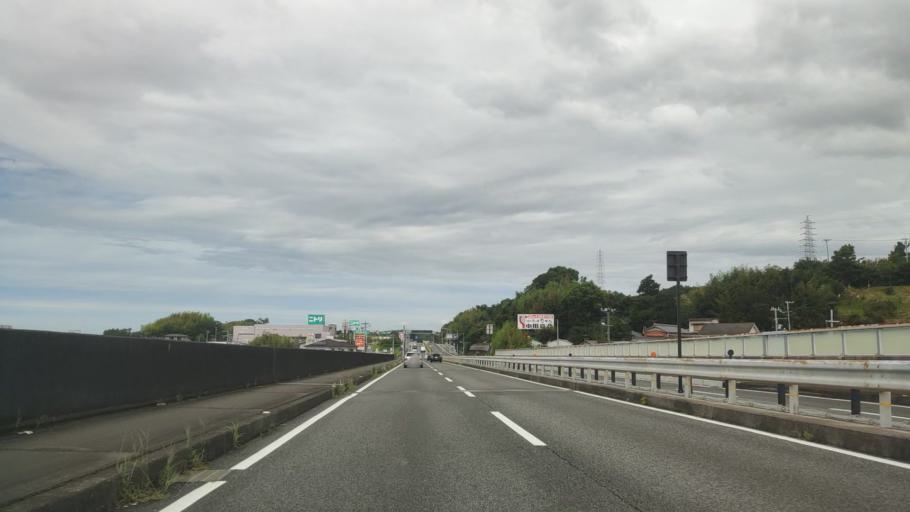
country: JP
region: Wakayama
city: Tanabe
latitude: 33.7189
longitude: 135.4068
